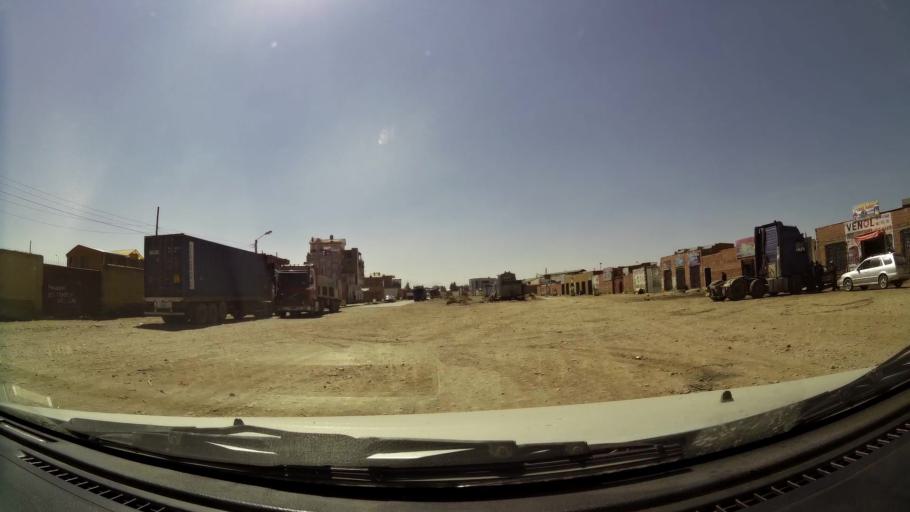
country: BO
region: La Paz
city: La Paz
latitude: -16.5492
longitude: -68.1826
